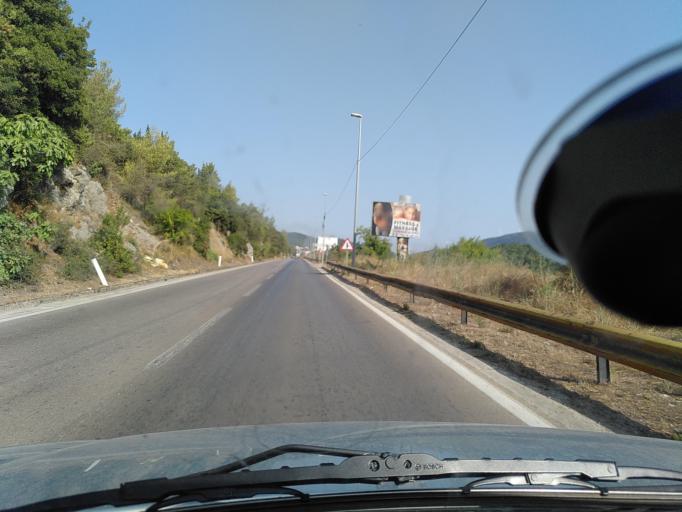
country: ME
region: Ulcinj
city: Ulcinj
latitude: 41.9396
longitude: 19.2154
